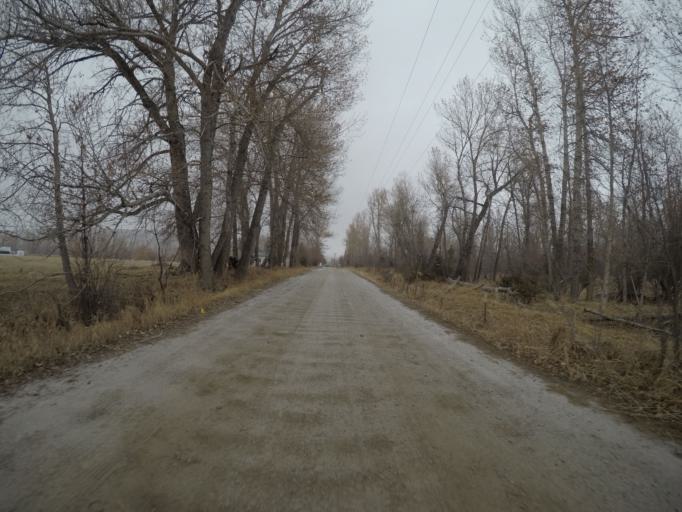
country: US
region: Montana
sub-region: Stillwater County
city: Absarokee
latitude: 45.5281
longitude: -109.4386
